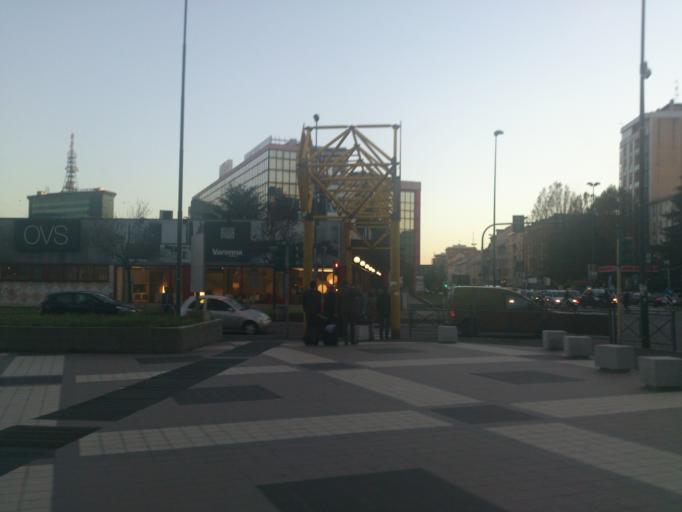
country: IT
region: Lombardy
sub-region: Citta metropolitana di Milano
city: Sesto San Giovanni
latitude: 45.5269
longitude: 9.2292
